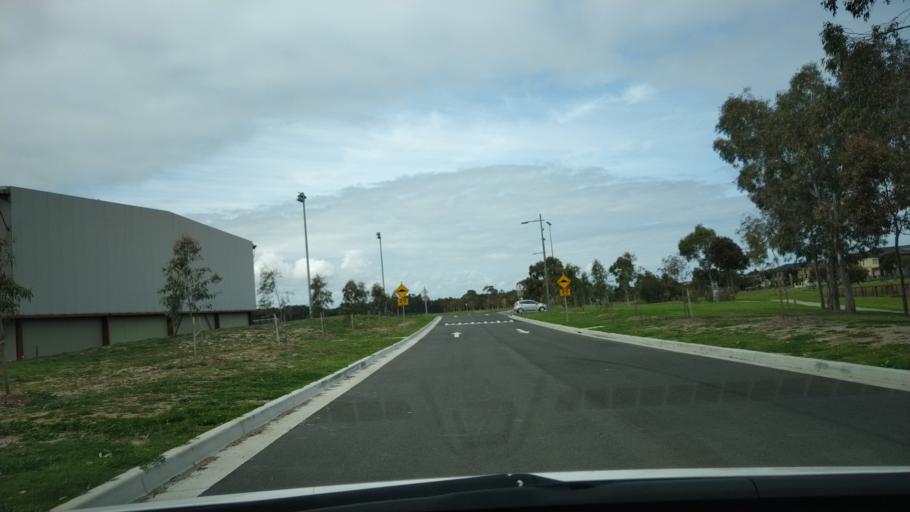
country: AU
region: Victoria
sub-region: Greater Dandenong
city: Keysborough
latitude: -37.9956
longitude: 145.1533
